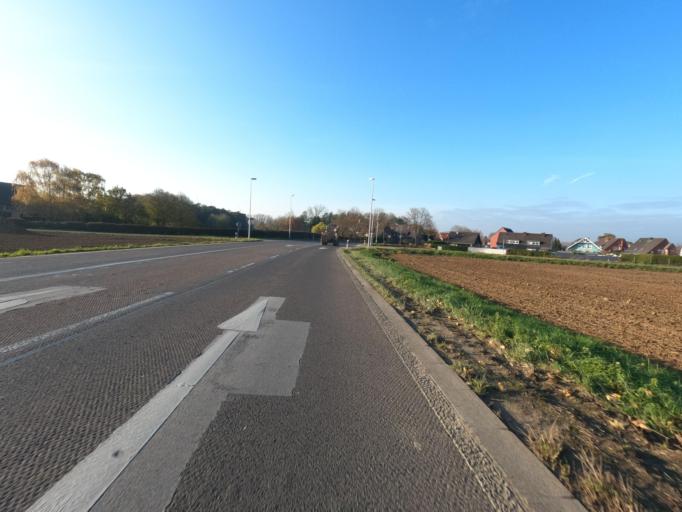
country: DE
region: North Rhine-Westphalia
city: Huckelhoven
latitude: 51.0108
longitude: 6.1887
